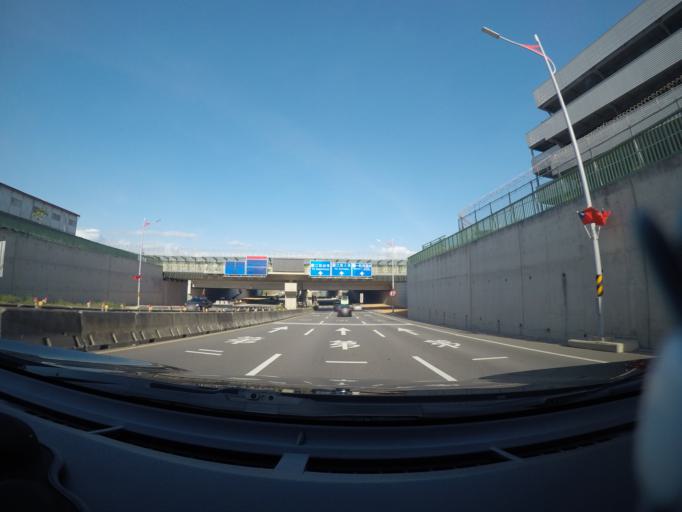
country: TW
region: Taiwan
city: Taoyuan City
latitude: 25.0678
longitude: 121.2227
